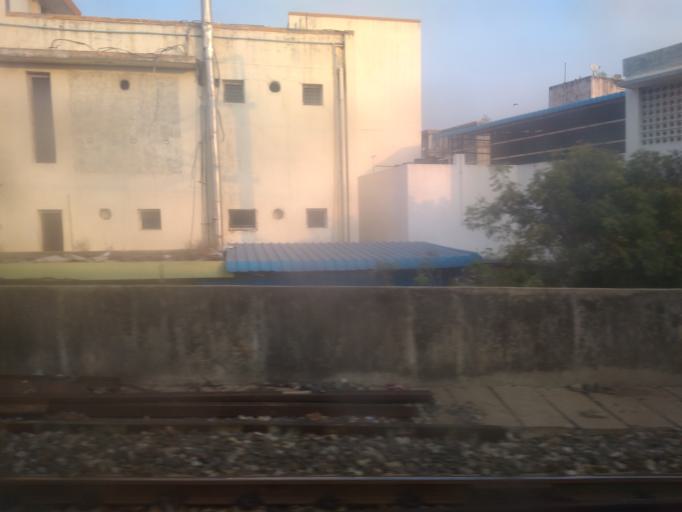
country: IN
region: Tamil Nadu
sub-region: Chennai
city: Gandhi Nagar
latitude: 13.0366
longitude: 80.2687
